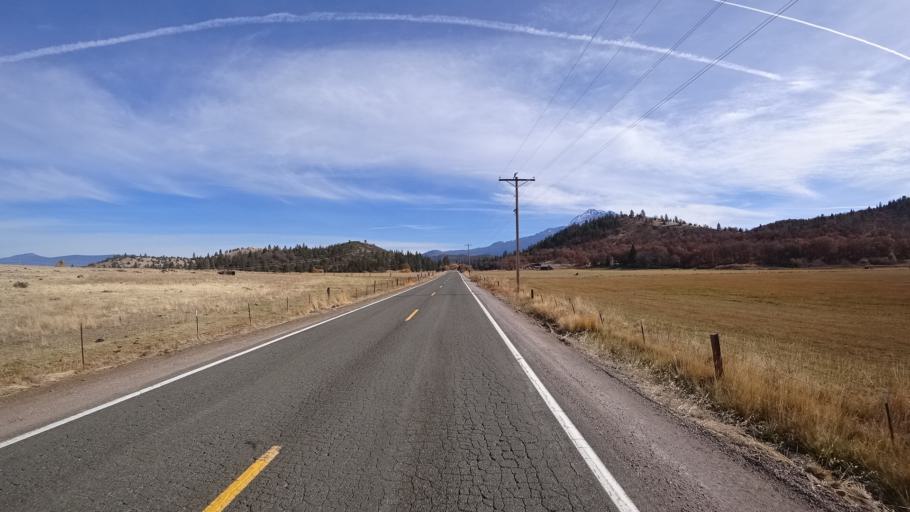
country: US
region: California
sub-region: Siskiyou County
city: Weed
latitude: 41.4678
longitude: -122.4194
